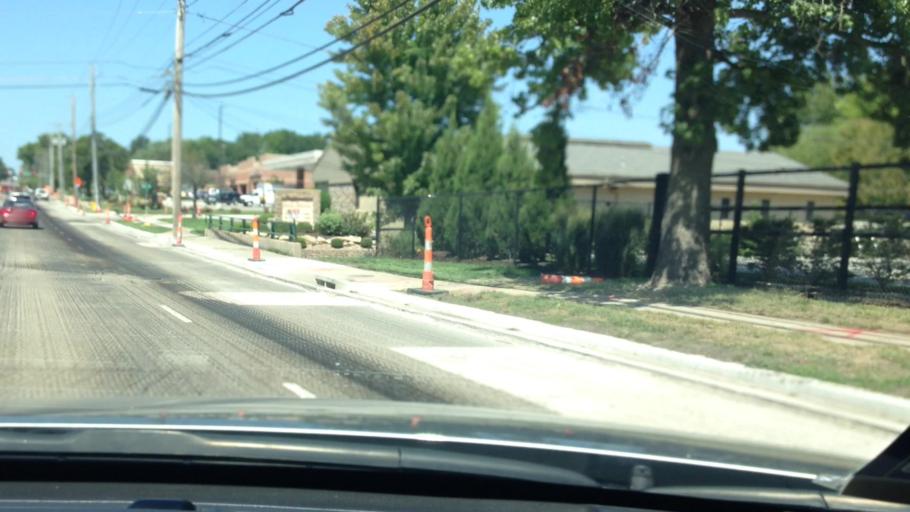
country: US
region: Kansas
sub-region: Johnson County
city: Overland Park
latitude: 38.9539
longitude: -94.6862
